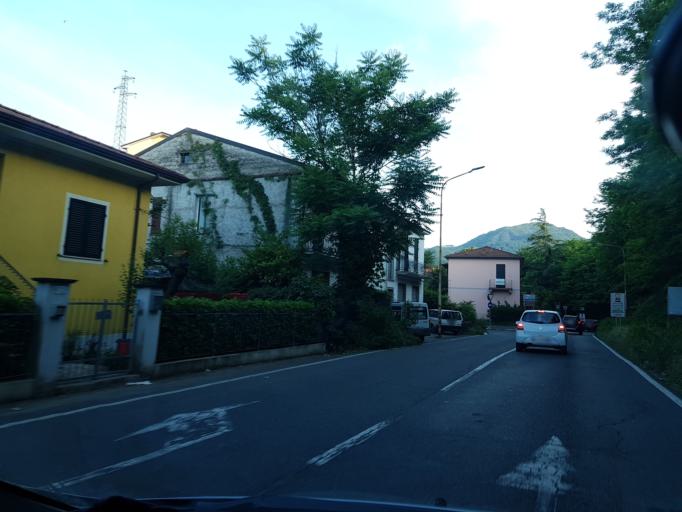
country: IT
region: Tuscany
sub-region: Provincia di Massa-Carrara
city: Aulla
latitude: 44.2178
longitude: 9.9683
